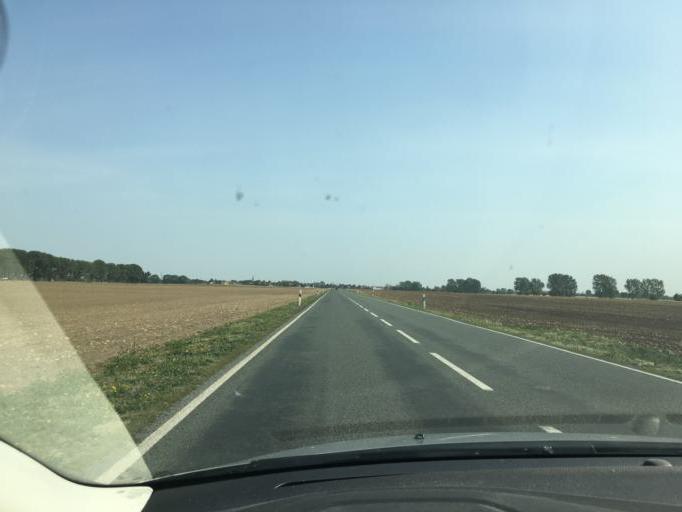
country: DE
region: Saxony-Anhalt
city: Plotzky
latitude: 52.0024
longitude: 11.8143
